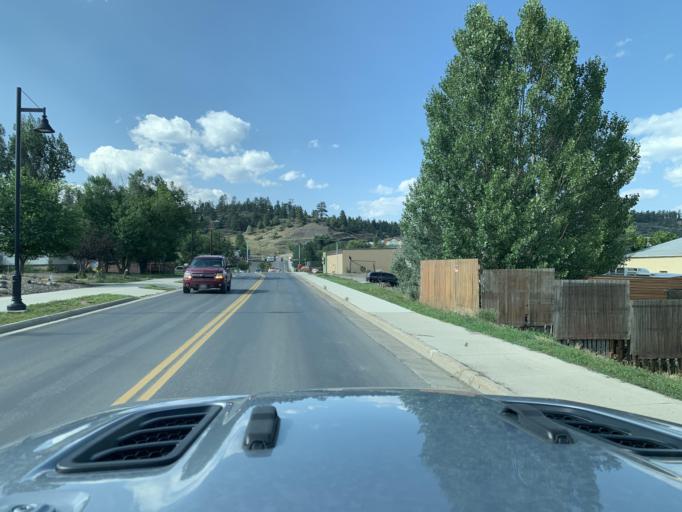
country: US
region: Colorado
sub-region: Archuleta County
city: Pagosa Springs
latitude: 37.2649
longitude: -107.0171
